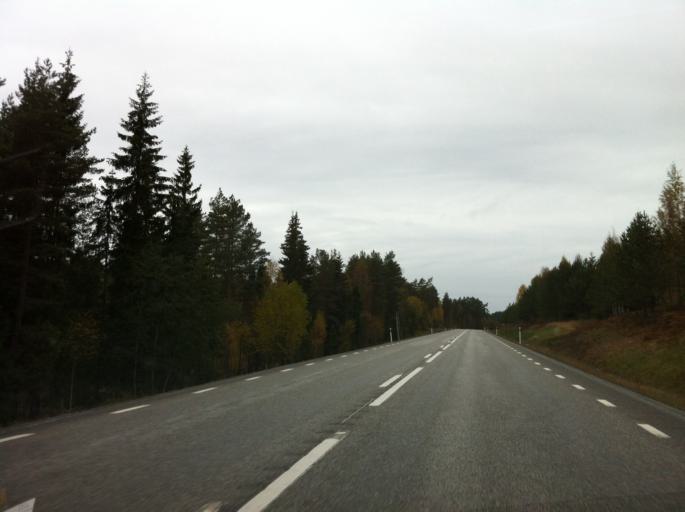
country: SE
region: OErebro
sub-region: Ljusnarsbergs Kommun
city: Kopparberg
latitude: 59.8804
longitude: 15.0297
